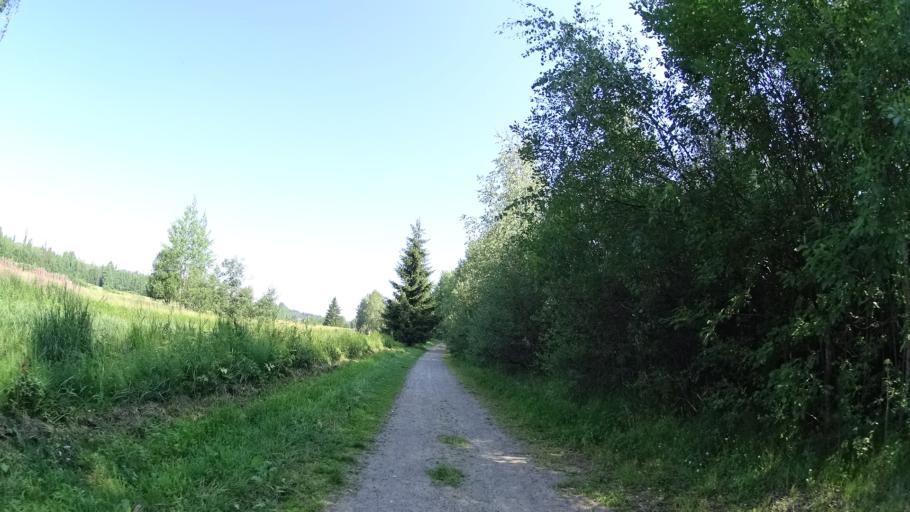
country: FI
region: Uusimaa
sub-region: Helsinki
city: Kerava
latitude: 60.3519
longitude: 25.1260
